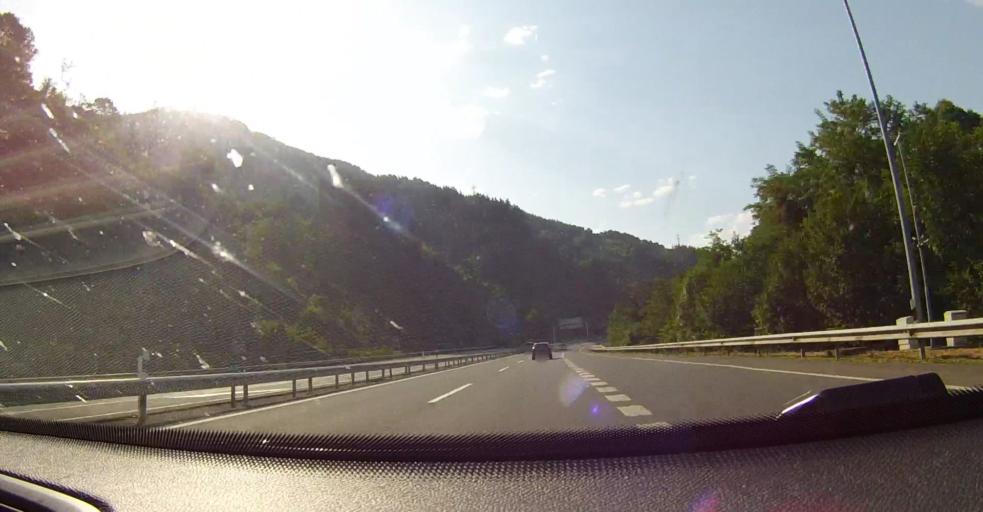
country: ES
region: Basque Country
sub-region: Provincia de Guipuzcoa
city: Elgoibar
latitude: 43.1918
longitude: -2.4330
